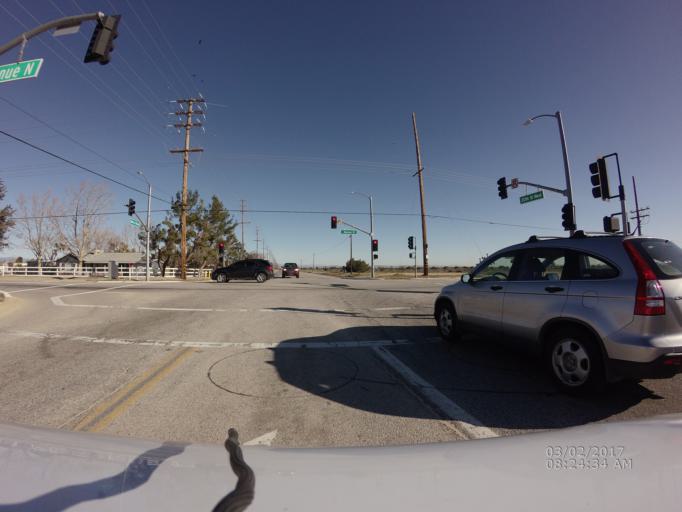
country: US
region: California
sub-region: Los Angeles County
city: Desert View Highlands
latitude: 34.6310
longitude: -118.1653
